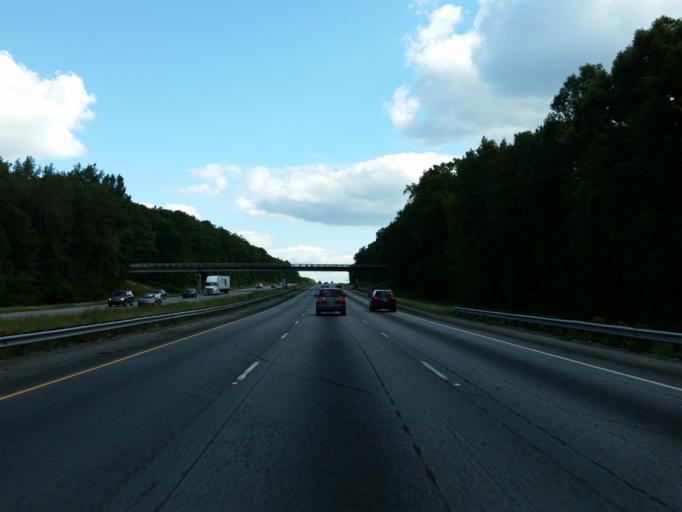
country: US
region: Georgia
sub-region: Henry County
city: Locust Grove
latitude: 33.3158
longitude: -84.1184
